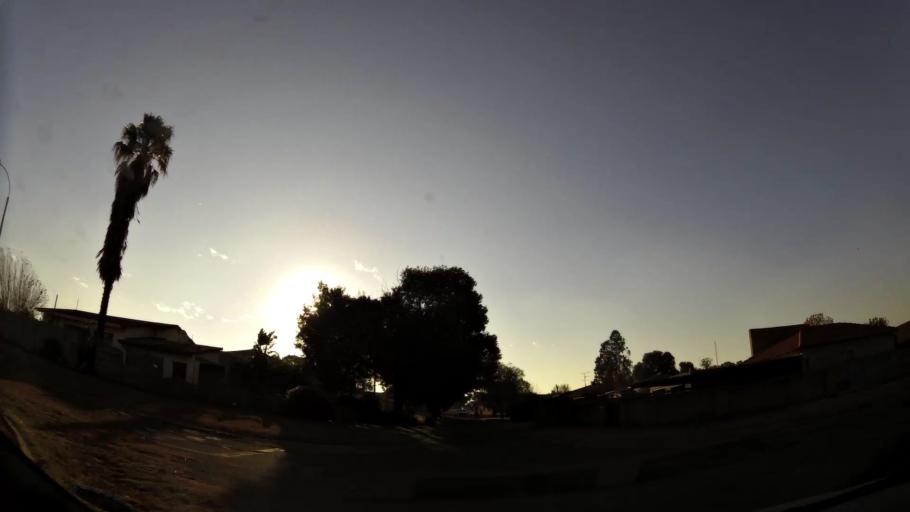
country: ZA
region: Gauteng
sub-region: West Rand District Municipality
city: Randfontein
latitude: -26.2246
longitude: 27.6462
